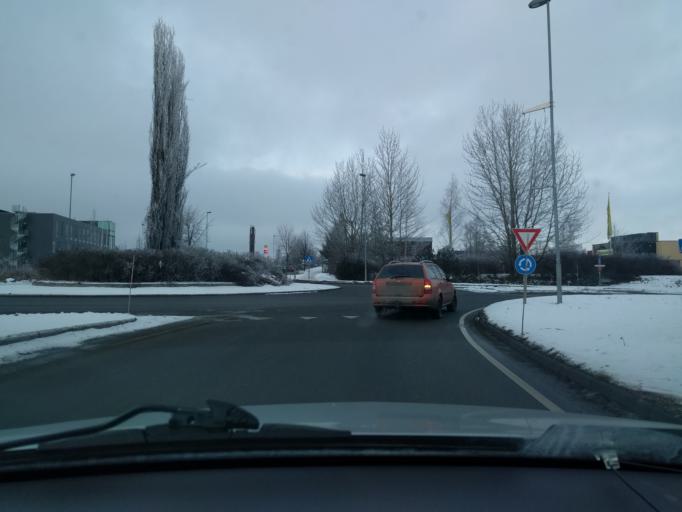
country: NO
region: Hedmark
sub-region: Hamar
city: Hamar
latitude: 60.7890
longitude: 11.0944
